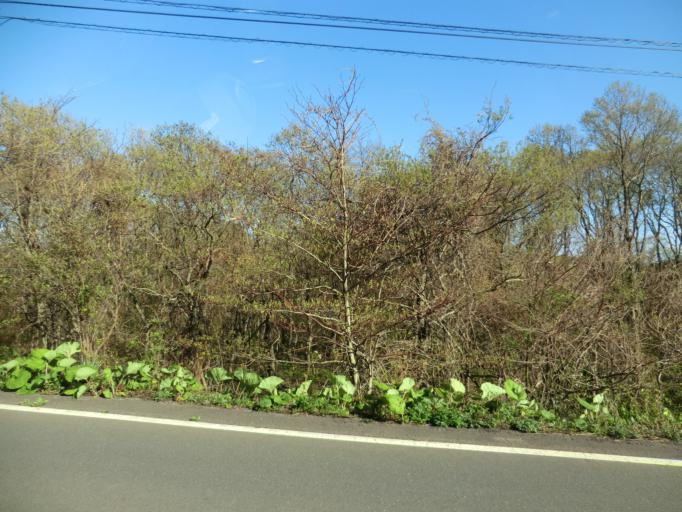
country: JP
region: Aomori
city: Mutsu
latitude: 41.2637
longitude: 141.3911
